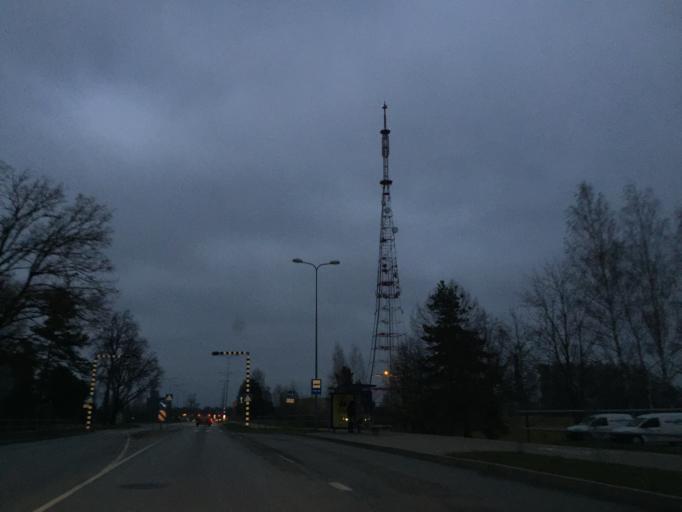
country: LV
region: Koceni
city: Koceni
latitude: 57.5253
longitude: 25.3790
